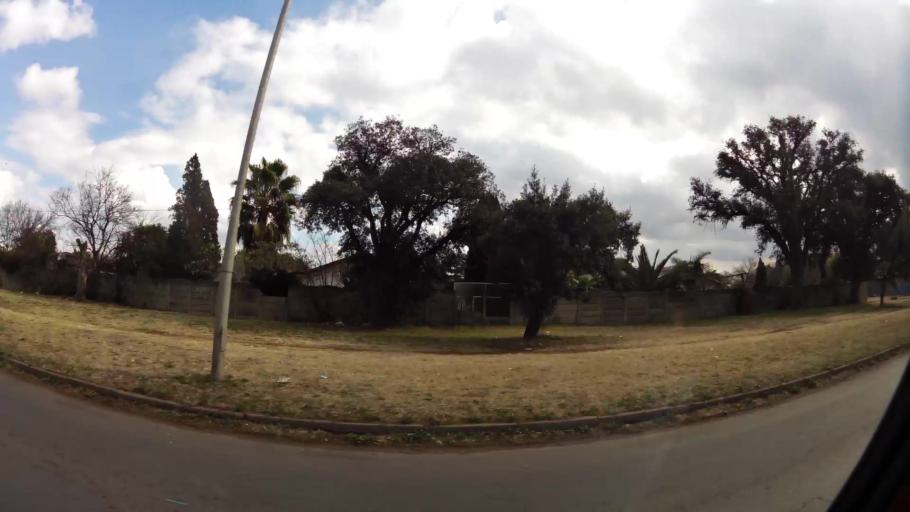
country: ZA
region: Gauteng
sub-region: Sedibeng District Municipality
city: Vanderbijlpark
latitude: -26.7107
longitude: 27.8360
